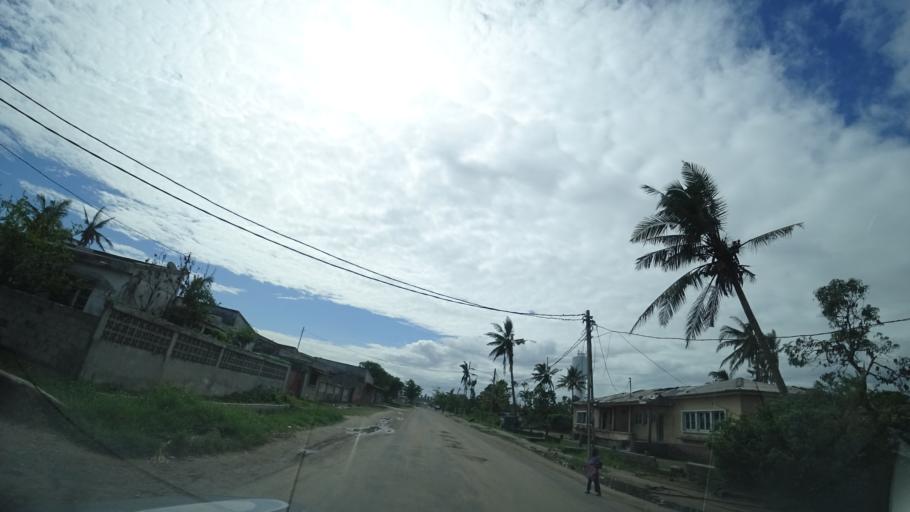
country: MZ
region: Sofala
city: Beira
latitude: -19.7603
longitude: 34.8650
